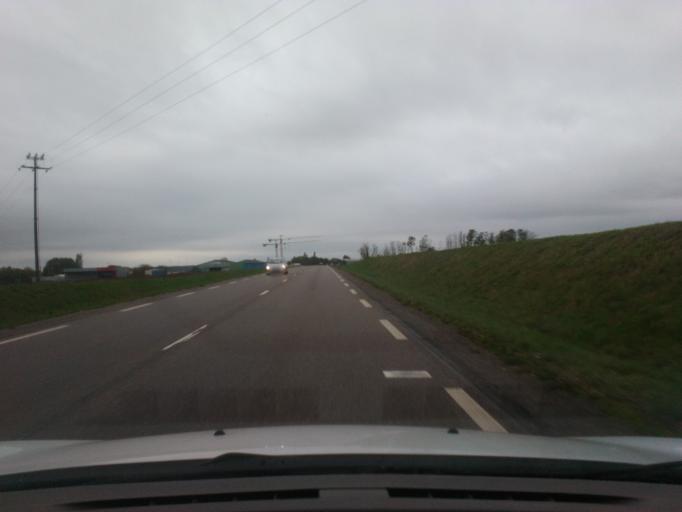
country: FR
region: Lorraine
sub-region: Departement des Vosges
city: Jeanmenil
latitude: 48.3395
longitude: 6.6644
